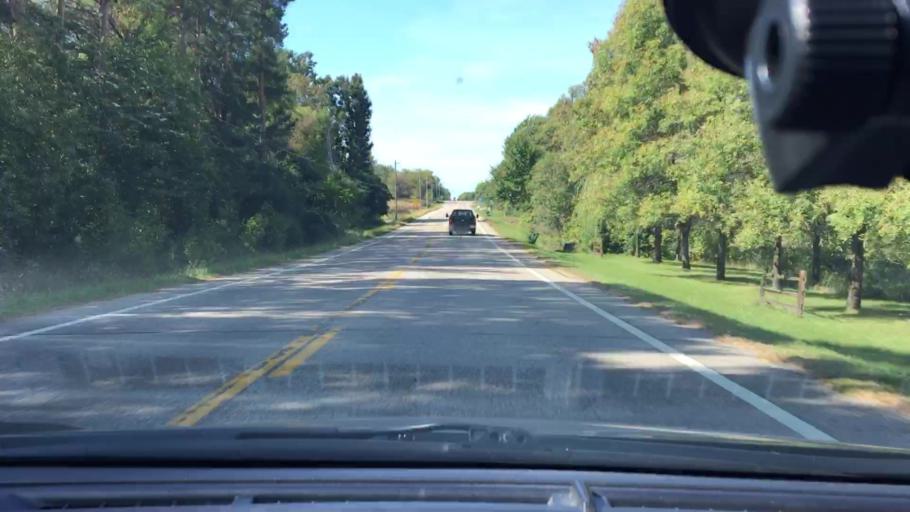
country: US
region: Minnesota
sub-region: Wright County
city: Hanover
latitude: 45.1236
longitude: -93.6284
